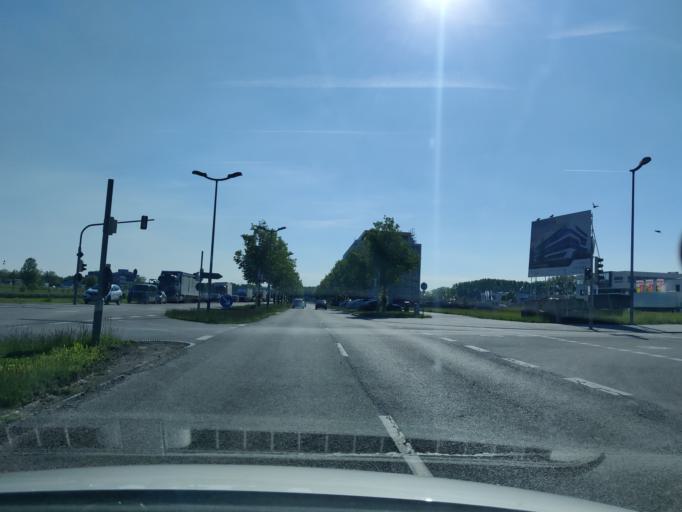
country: DE
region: Baden-Wuerttemberg
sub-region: Regierungsbezirk Stuttgart
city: Boeblingen
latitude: 48.6900
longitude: 8.9947
